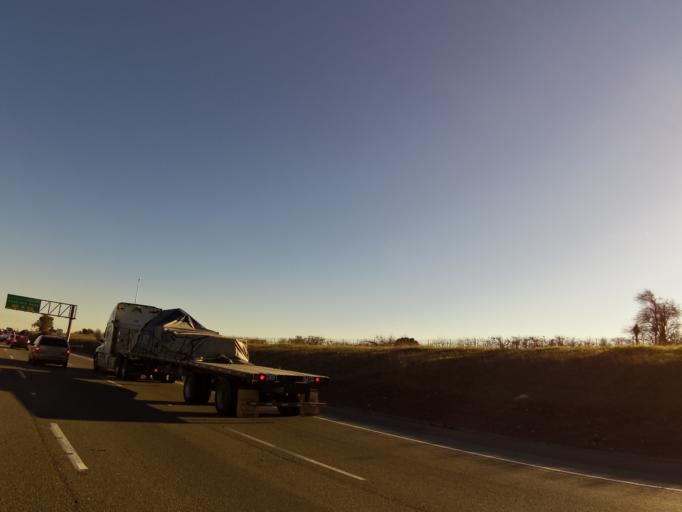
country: US
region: California
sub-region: Santa Clara County
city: Morgan Hill
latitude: 37.1618
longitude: -121.6624
